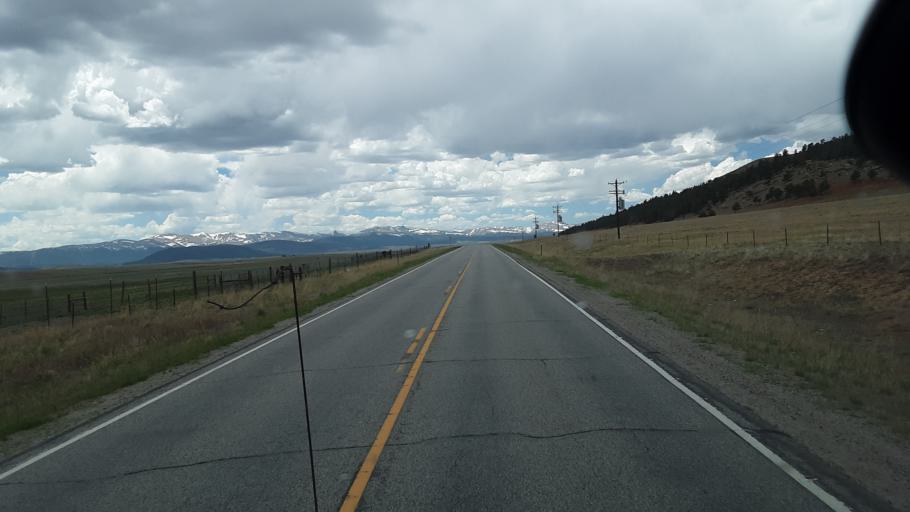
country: US
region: Colorado
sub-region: Park County
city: Fairplay
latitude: 39.0461
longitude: -105.8378
